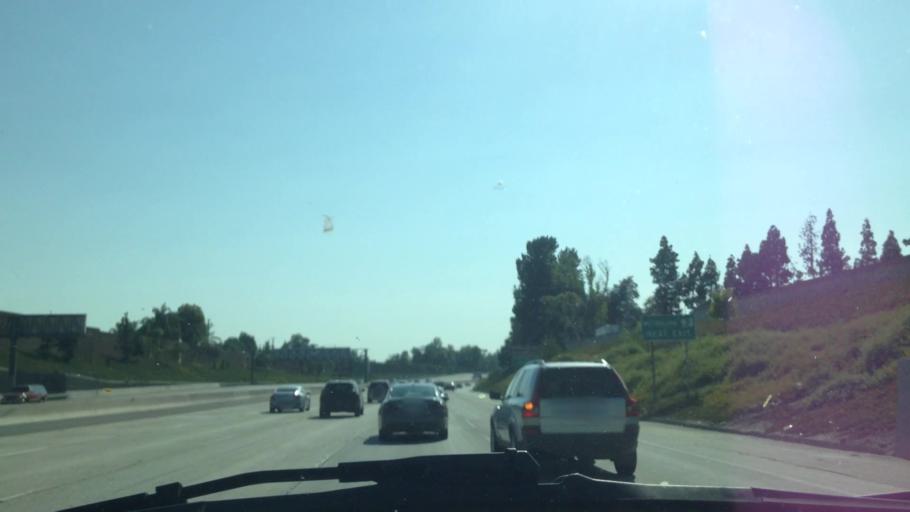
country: US
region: California
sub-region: Orange County
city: Orange
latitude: 33.7762
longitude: -117.8446
